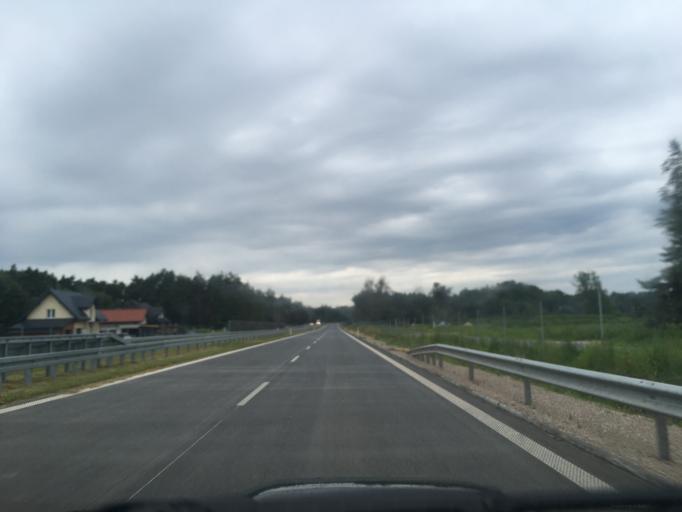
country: PL
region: Masovian Voivodeship
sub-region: Powiat piaseczynski
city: Gora Kalwaria
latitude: 51.9787
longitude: 21.1834
